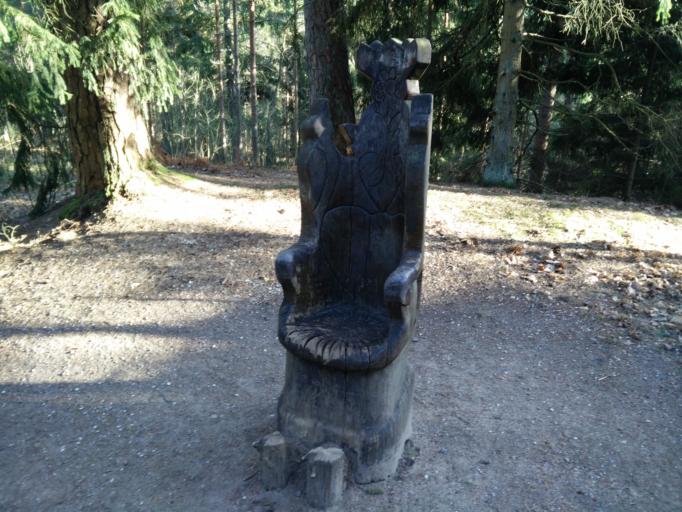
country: LT
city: Neringa
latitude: 55.5356
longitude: 21.1135
